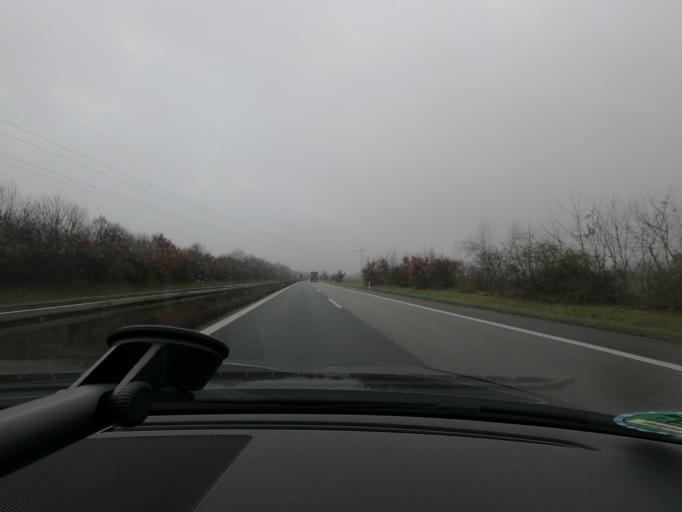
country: DE
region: Bavaria
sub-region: Upper Franconia
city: Eggolsheim
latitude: 49.7623
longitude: 11.0539
